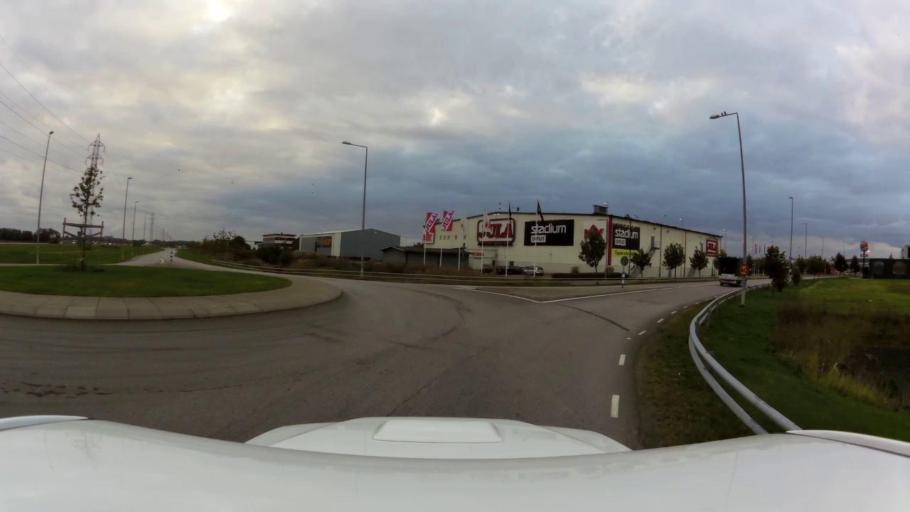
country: SE
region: OEstergoetland
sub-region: Linkopings Kommun
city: Linkoping
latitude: 58.4359
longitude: 15.5927
